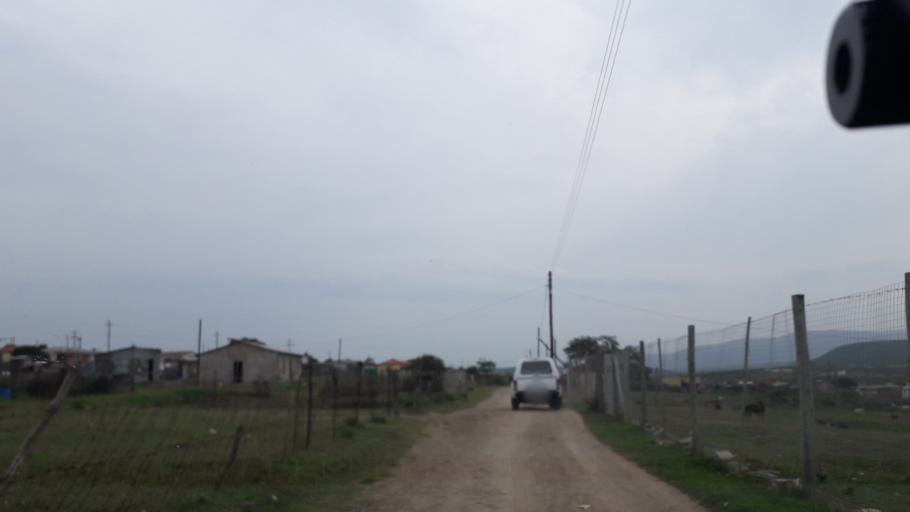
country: ZA
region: Eastern Cape
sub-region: Buffalo City Metropolitan Municipality
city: Bhisho
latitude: -32.8358
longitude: 27.3715
